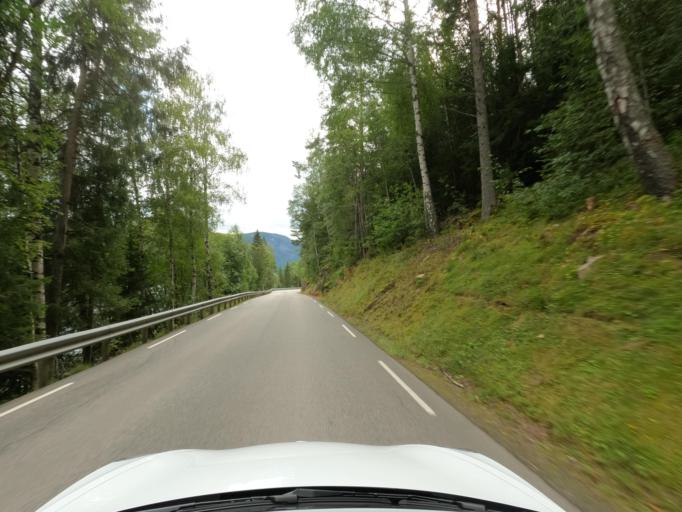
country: NO
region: Telemark
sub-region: Tinn
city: Rjukan
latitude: 59.9681
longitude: 8.8089
